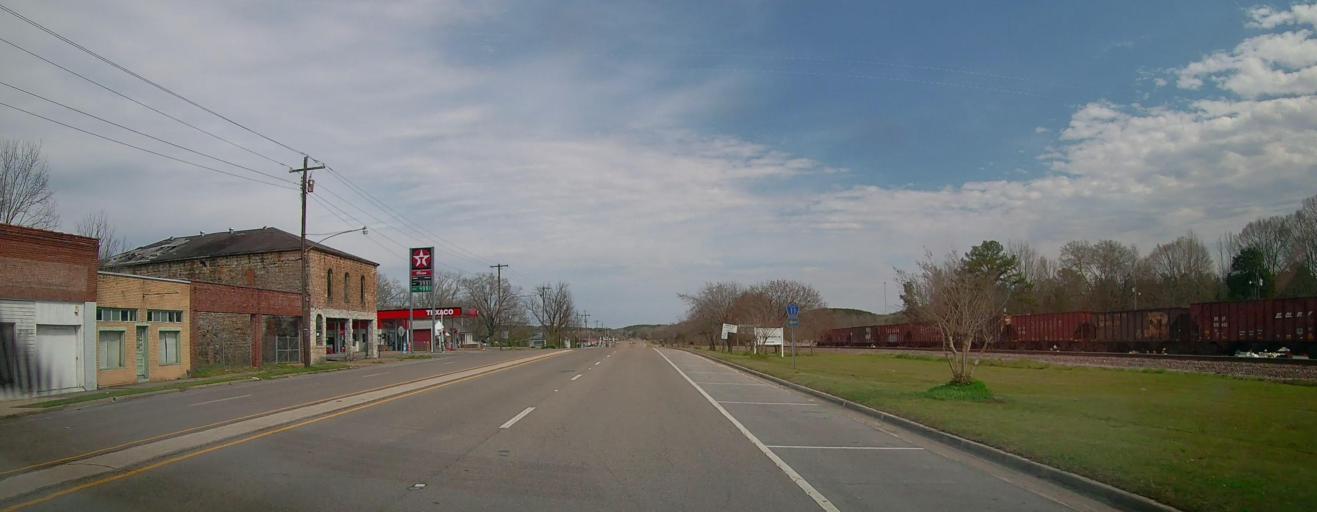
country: US
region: Alabama
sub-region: Walker County
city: Carbon Hill
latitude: 33.8885
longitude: -87.5289
